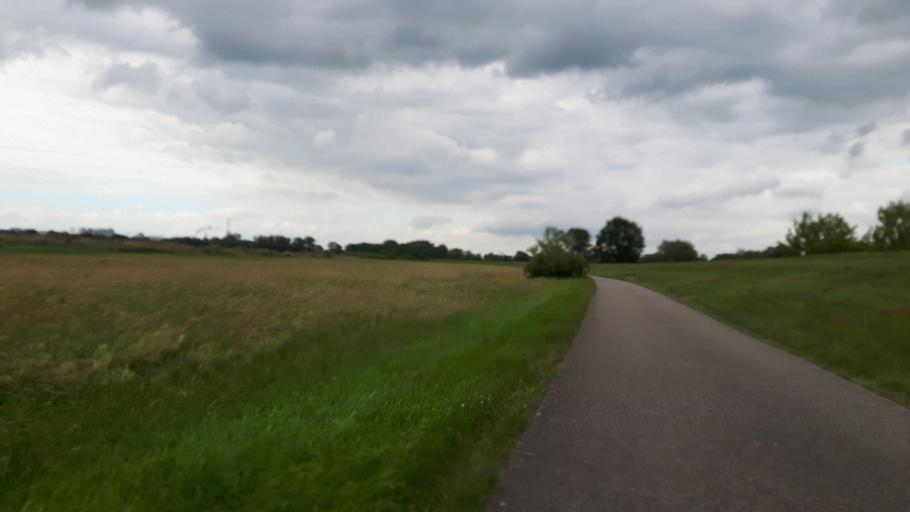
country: DE
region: Brandenburg
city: Schwedt (Oder)
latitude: 53.0618
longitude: 14.3149
